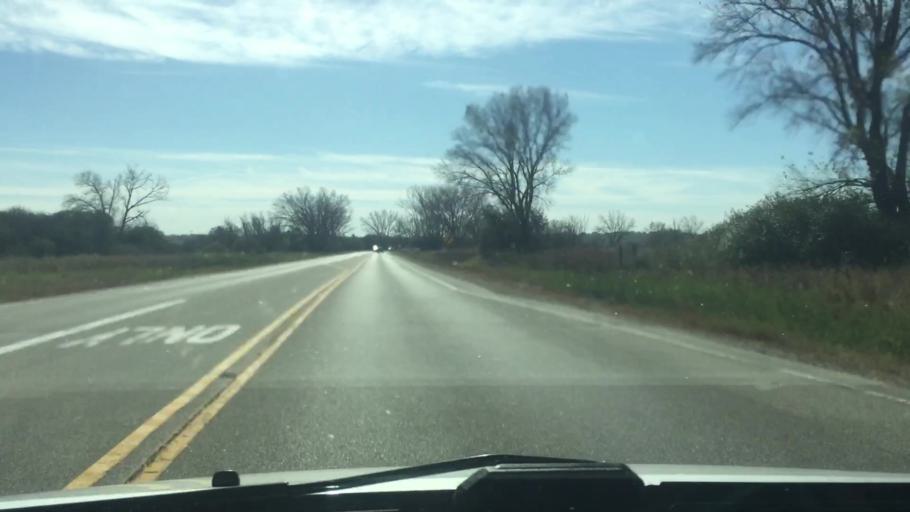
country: US
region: Wisconsin
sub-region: Waukesha County
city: Pewaukee
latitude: 43.0567
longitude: -88.2521
